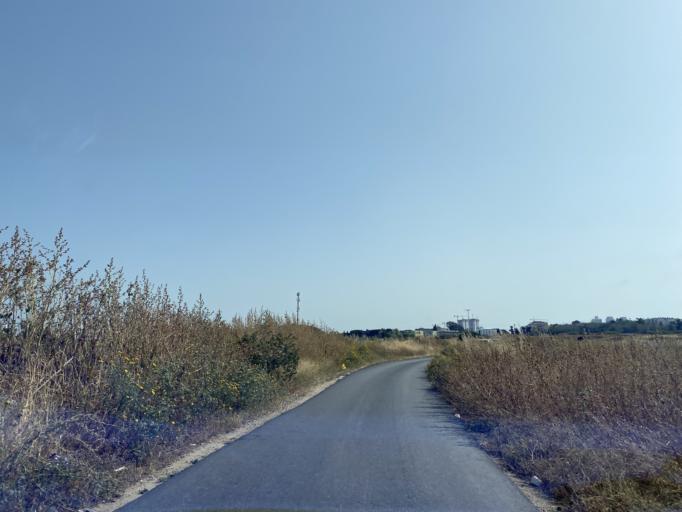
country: IL
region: Central District
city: Netanya
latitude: 32.3072
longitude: 34.8625
